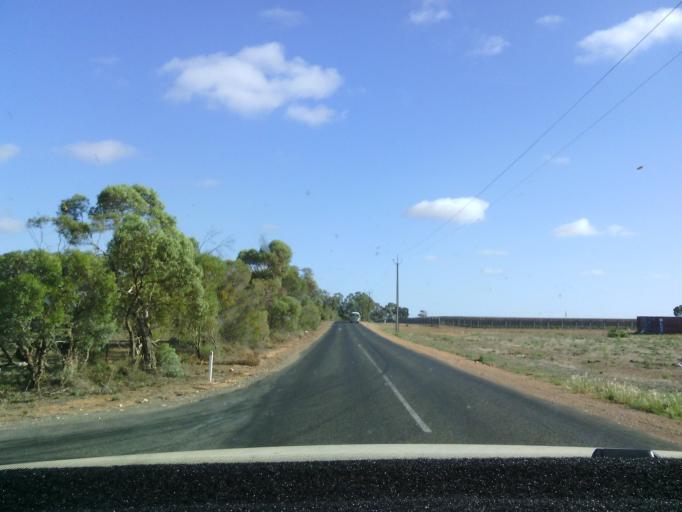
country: AU
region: South Australia
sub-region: Berri and Barmera
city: Monash
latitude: -34.2565
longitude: 140.5411
